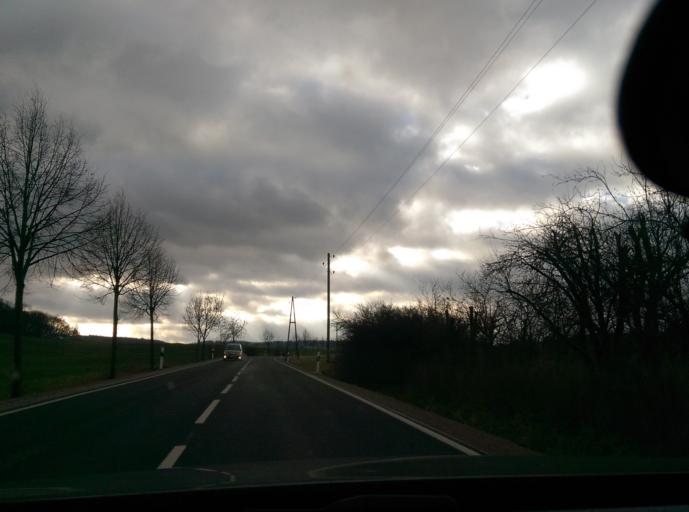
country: DE
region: Thuringia
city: Krauthausen
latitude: 51.0231
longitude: 10.2604
